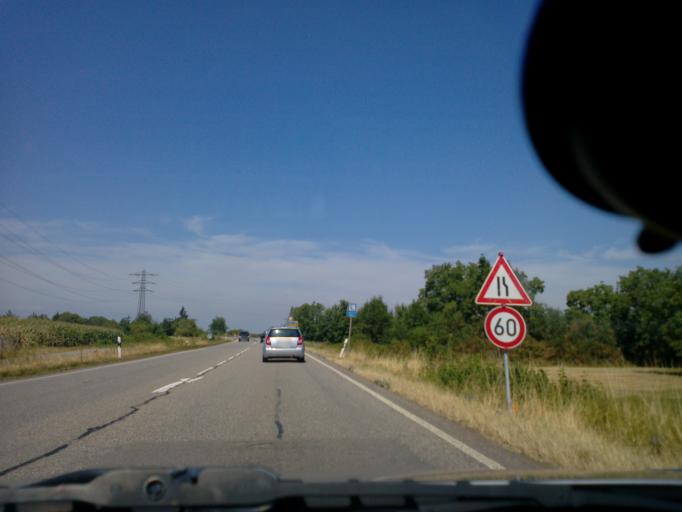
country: DE
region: Baden-Wuerttemberg
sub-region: Freiburg Region
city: Ortenberg
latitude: 48.4286
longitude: 7.9694
